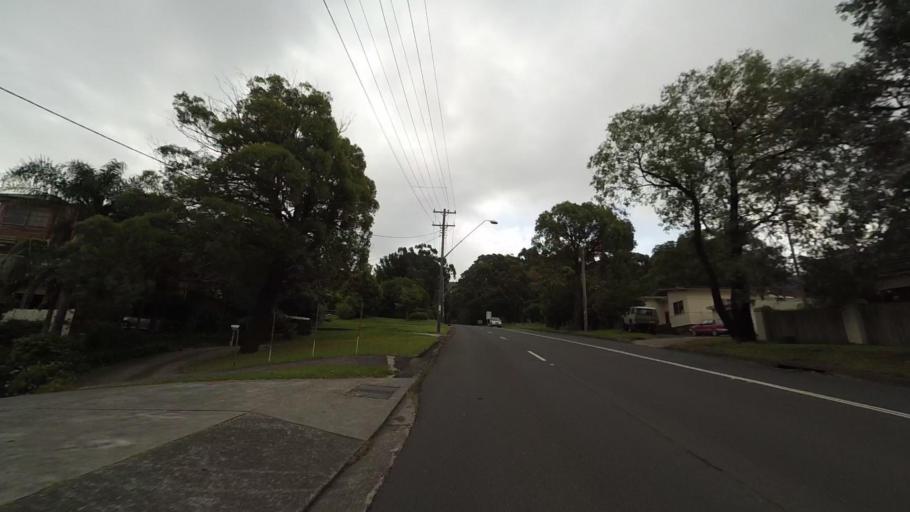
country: AU
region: New South Wales
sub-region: Wollongong
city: Bulli
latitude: -34.3205
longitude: 150.9079
